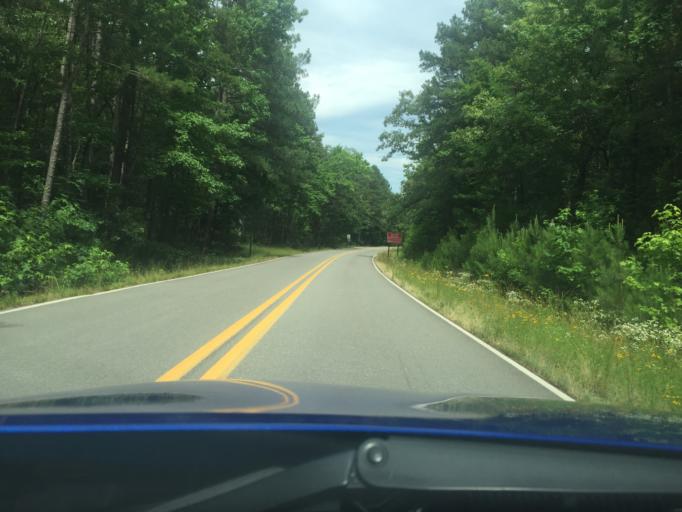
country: US
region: Arkansas
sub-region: Pulaski County
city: Maumelle
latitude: 34.8350
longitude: -92.4589
